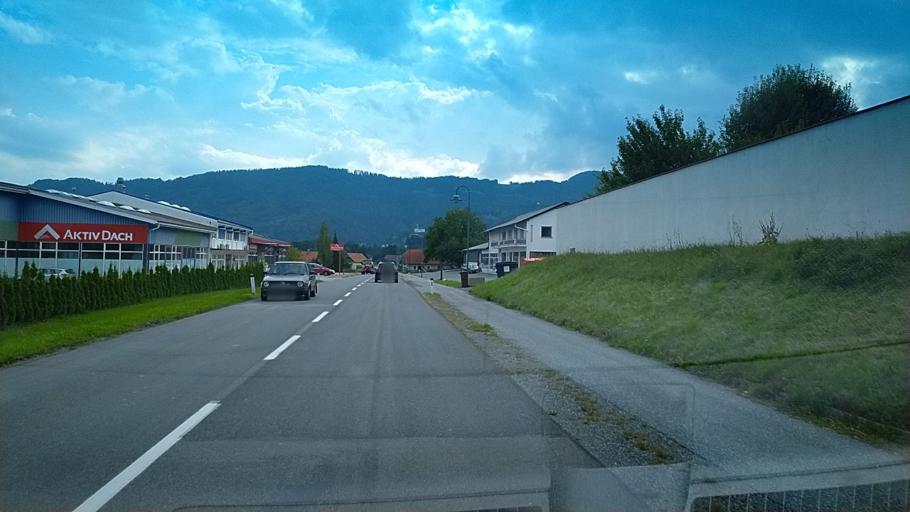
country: AT
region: Styria
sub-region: Politischer Bezirk Deutschlandsberg
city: Schwanberg
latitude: 46.7709
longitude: 15.2123
